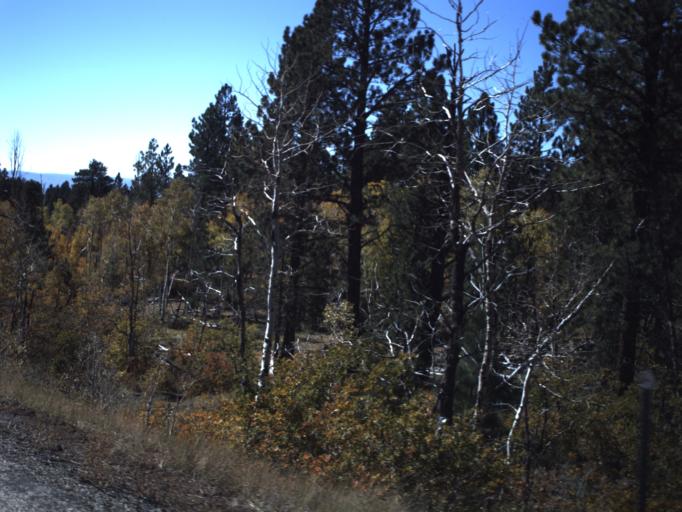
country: US
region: Utah
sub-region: Wayne County
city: Loa
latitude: 38.0067
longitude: -111.4052
